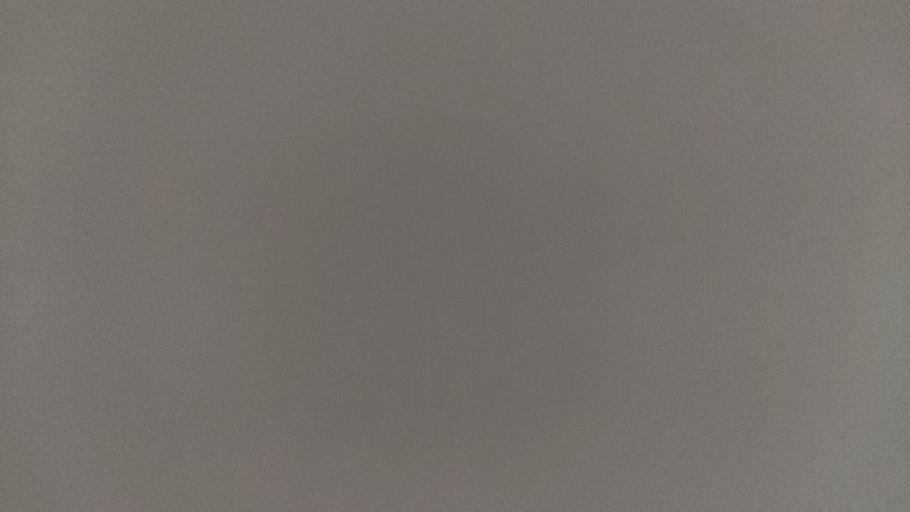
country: RU
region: Moskovskaya
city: Rogachevo
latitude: 56.4401
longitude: 37.1596
